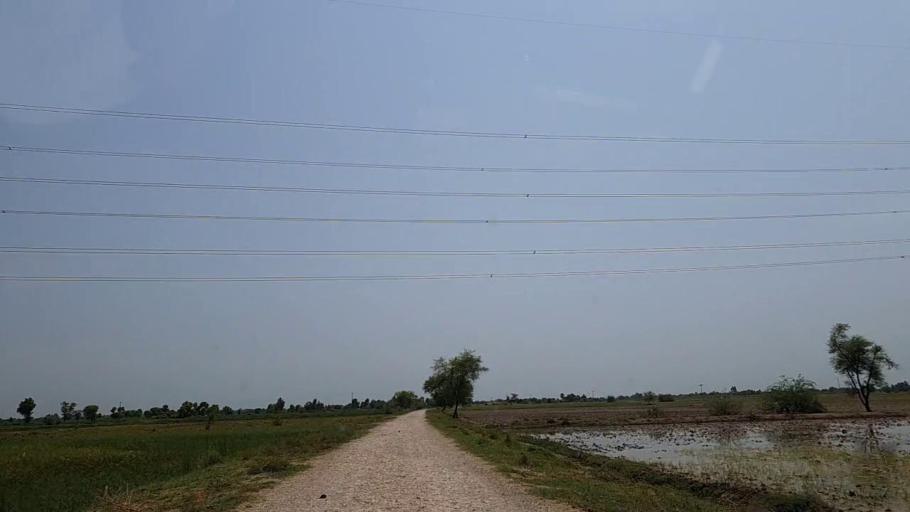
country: PK
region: Sindh
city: Ghotki
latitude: 27.9941
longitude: 69.4106
